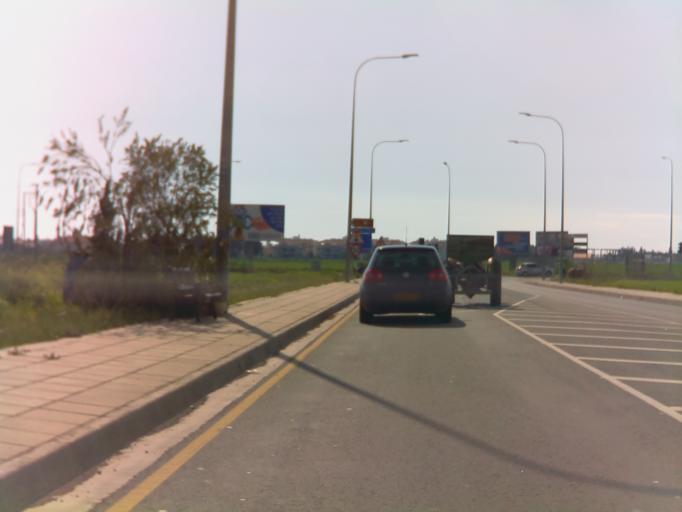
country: CY
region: Larnaka
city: Meneou
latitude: 34.8689
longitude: 33.5981
